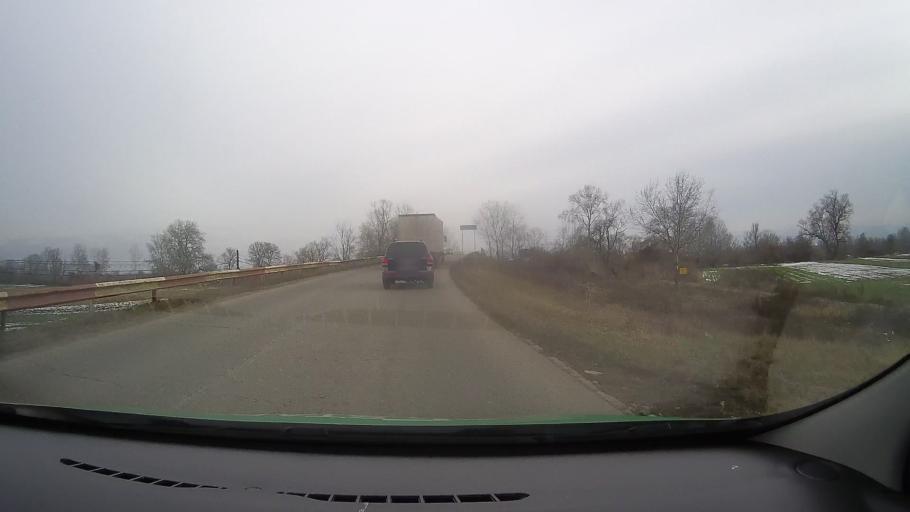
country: RO
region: Hunedoara
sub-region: Comuna Geoagiu
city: Geoagiu
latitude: 45.9064
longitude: 23.2194
